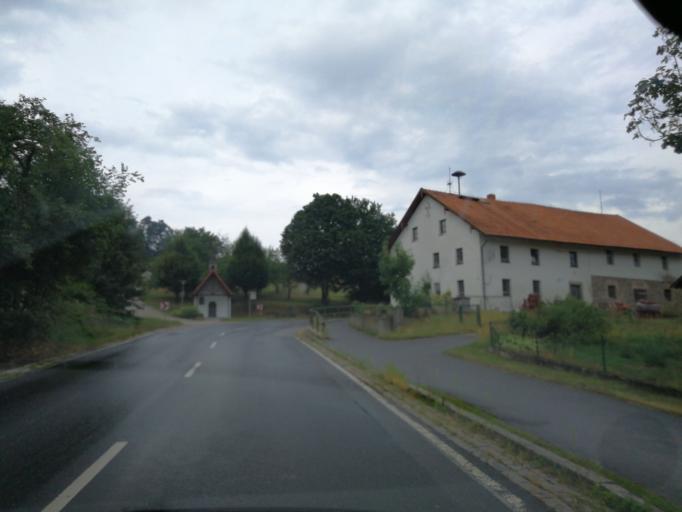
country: DE
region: Bavaria
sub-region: Upper Palatinate
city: Schorndorf
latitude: 49.1654
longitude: 12.6075
